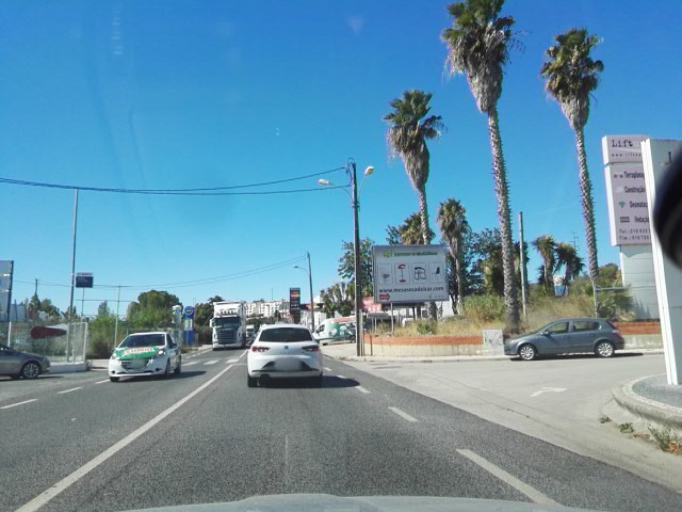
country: PT
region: Lisbon
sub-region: Vila Franca de Xira
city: Sobralinho
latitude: 38.9070
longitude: -9.0314
